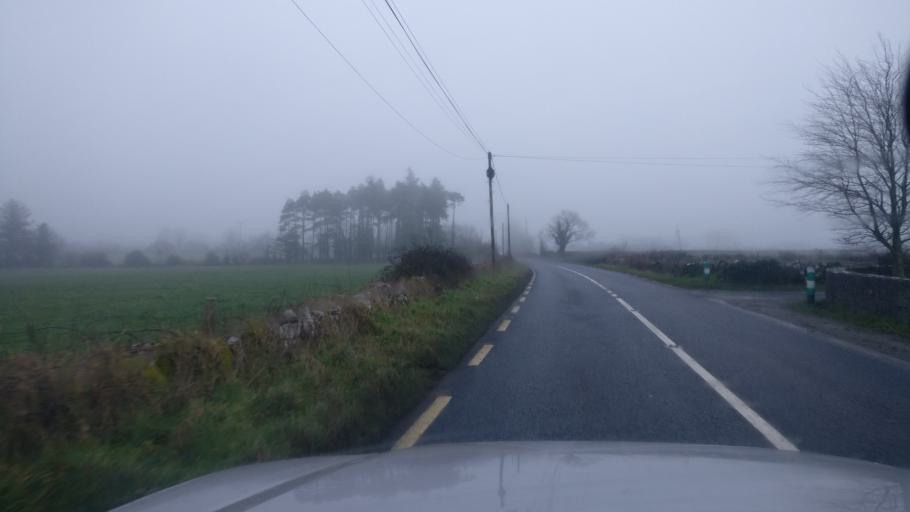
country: IE
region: Connaught
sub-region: County Galway
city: Loughrea
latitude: 53.1847
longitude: -8.6349
